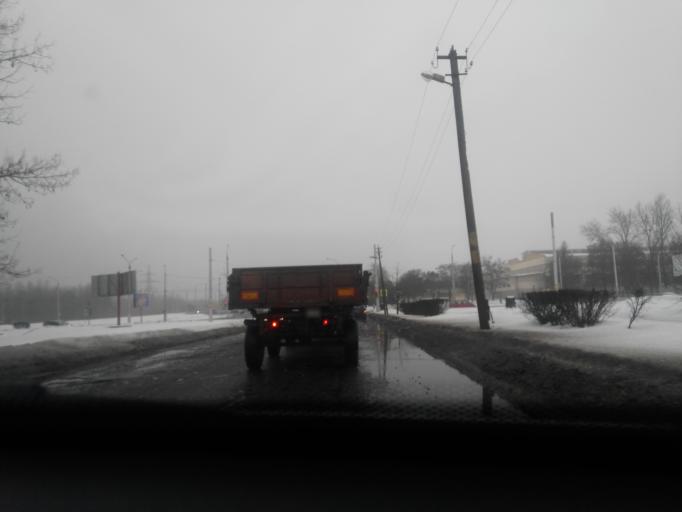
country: BY
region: Mogilev
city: Babruysk
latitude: 53.1847
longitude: 29.2144
